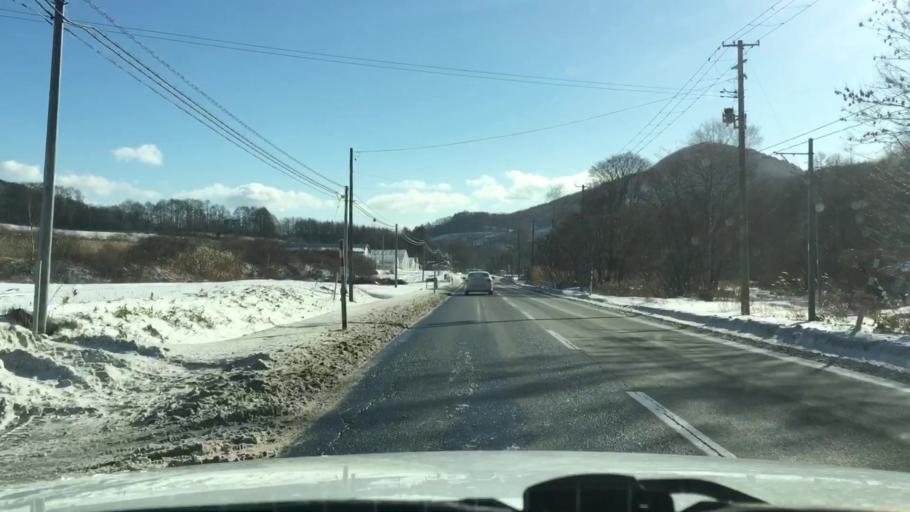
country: JP
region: Iwate
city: Morioka-shi
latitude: 39.6449
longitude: 141.3694
